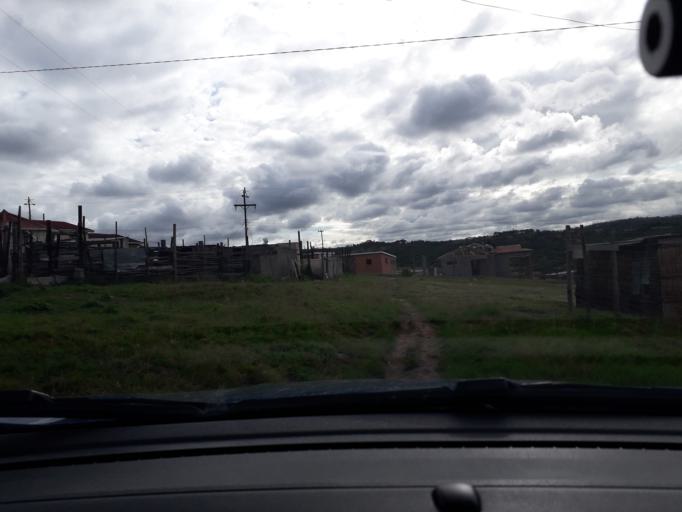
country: ZA
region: Eastern Cape
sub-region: Buffalo City Metropolitan Municipality
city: East London
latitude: -32.8507
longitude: 27.9857
